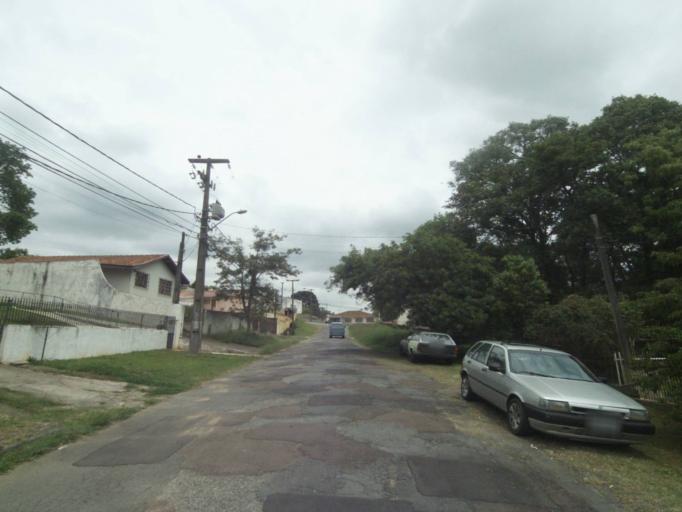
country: BR
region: Parana
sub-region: Curitiba
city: Curitiba
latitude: -25.3924
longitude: -49.2897
